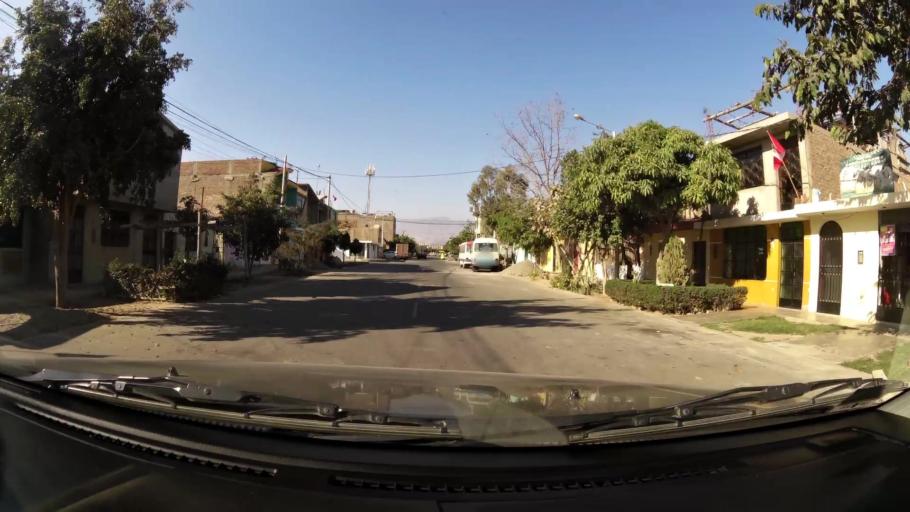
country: PE
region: Ica
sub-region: Provincia de Ica
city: La Tinguina
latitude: -14.0447
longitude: -75.7048
